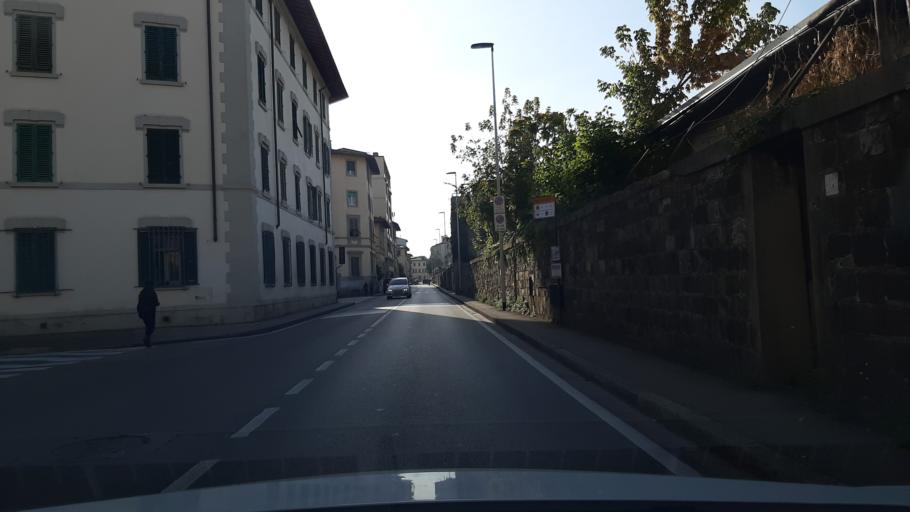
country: IT
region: Tuscany
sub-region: Province of Florence
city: Fiesole
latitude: 43.7746
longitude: 11.2812
